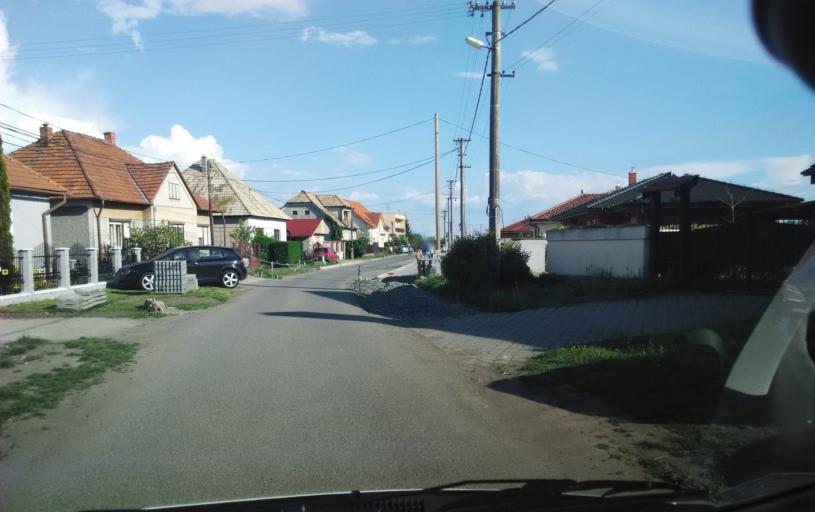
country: SK
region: Nitriansky
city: Levice
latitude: 48.2412
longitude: 18.5783
